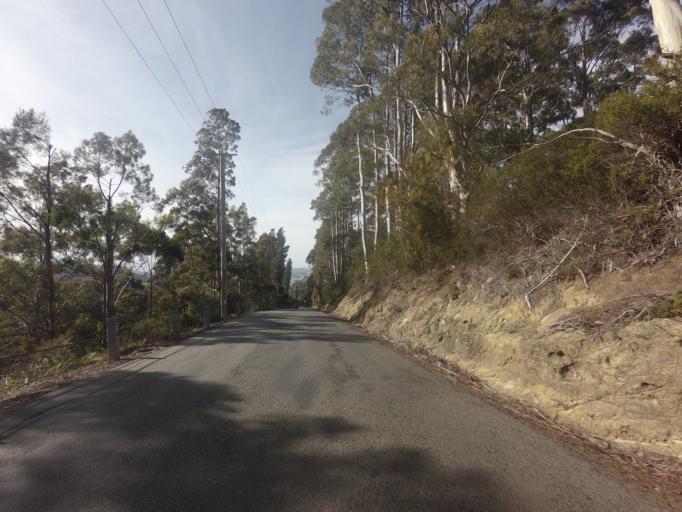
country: AU
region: Tasmania
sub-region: Kingborough
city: Kettering
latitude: -43.1671
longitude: 147.2106
